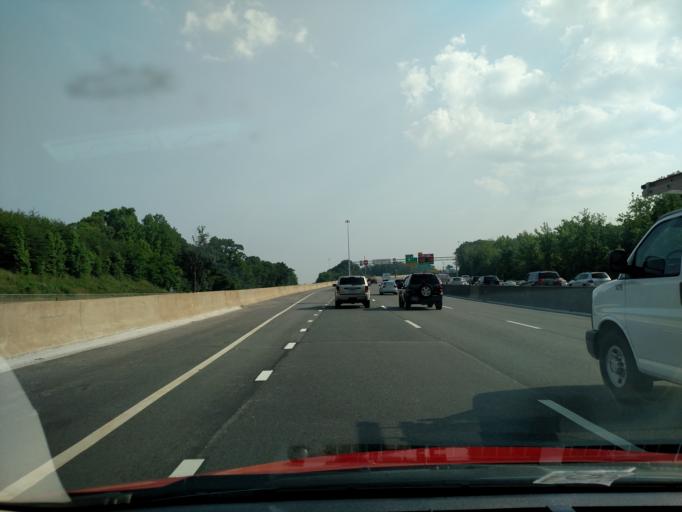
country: US
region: Virginia
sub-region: Fairfax County
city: Lorton
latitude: 38.6864
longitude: -77.2279
